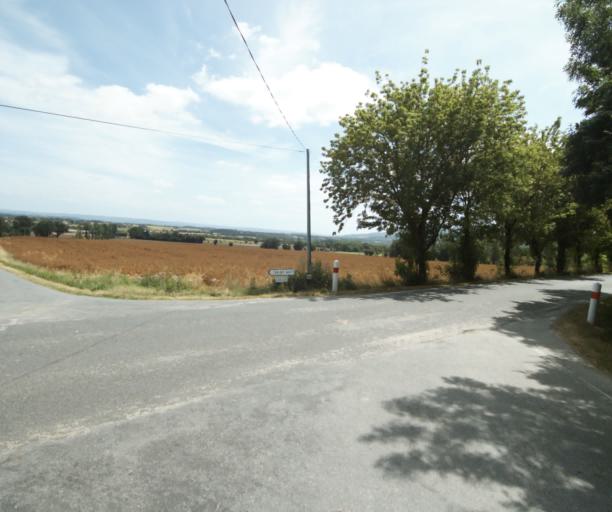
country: FR
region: Midi-Pyrenees
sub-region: Departement du Tarn
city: Dourgne
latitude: 43.5060
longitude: 2.0920
